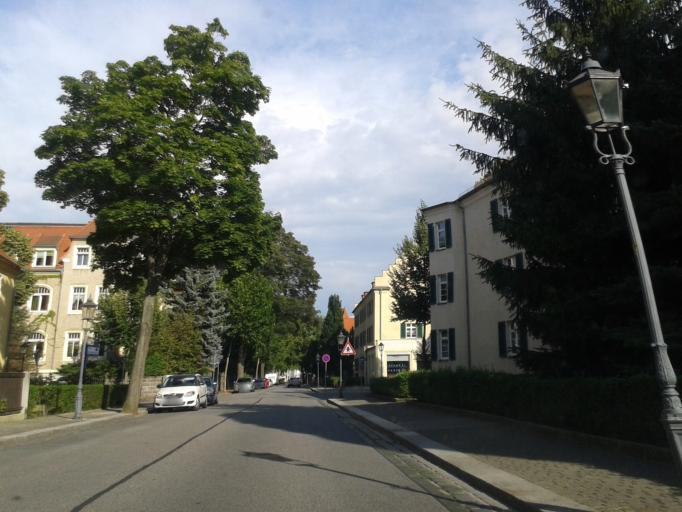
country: DE
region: Saxony
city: Dresden
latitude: 51.0954
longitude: 13.7152
